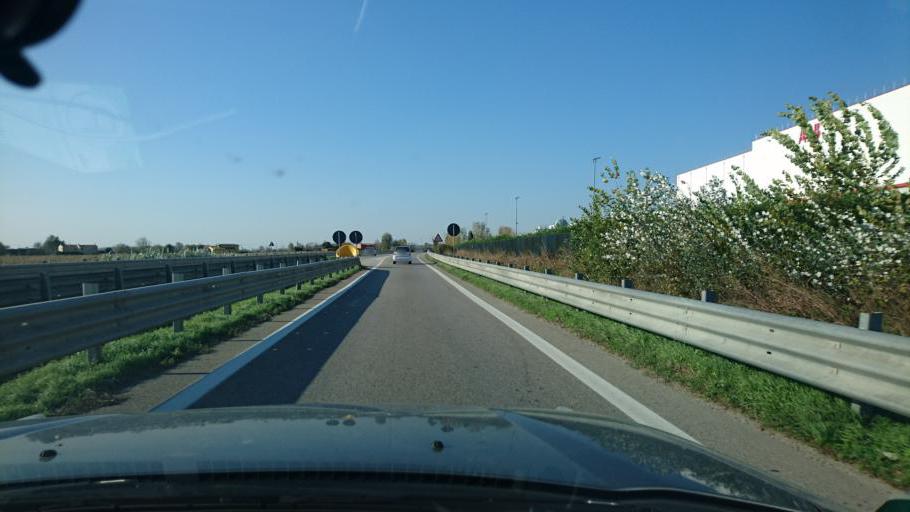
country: IT
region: Veneto
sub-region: Provincia di Padova
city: Monselice
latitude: 45.2075
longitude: 11.7437
